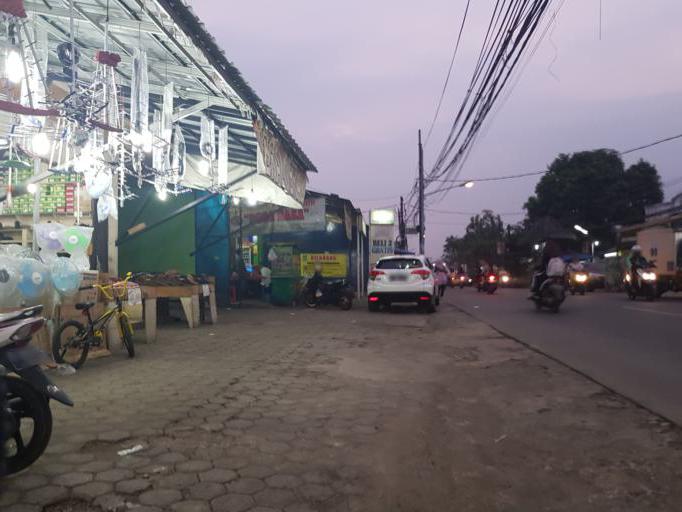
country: ID
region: West Java
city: Bekasi
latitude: -6.2935
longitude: 106.9193
